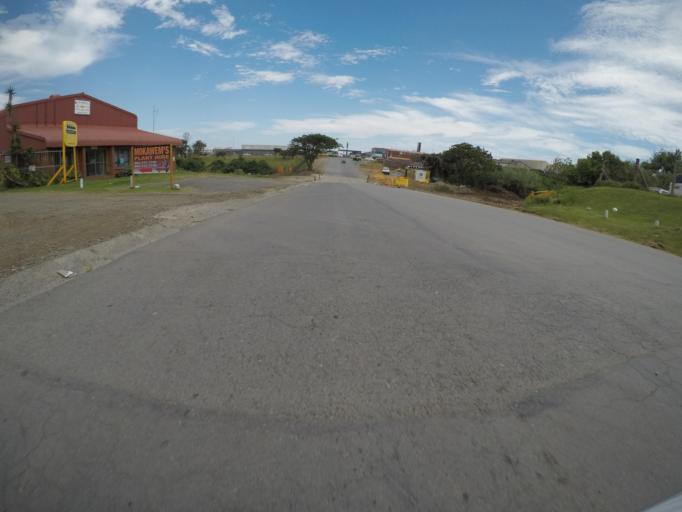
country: ZA
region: Eastern Cape
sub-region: Buffalo City Metropolitan Municipality
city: East London
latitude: -33.0330
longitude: 27.8804
